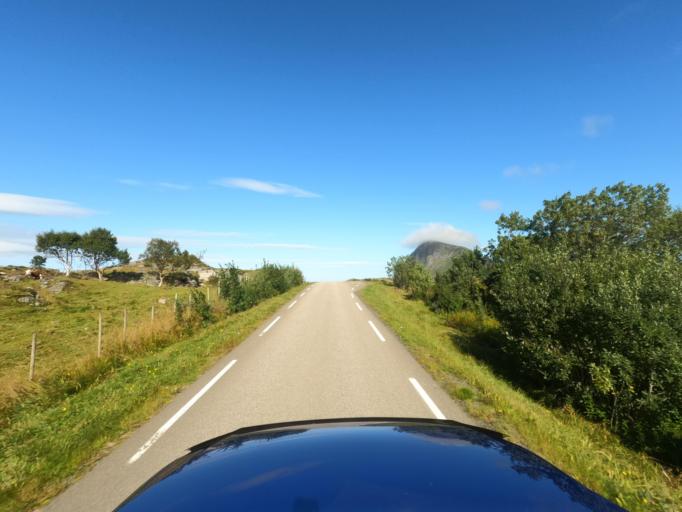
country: NO
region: Nordland
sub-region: Vestvagoy
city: Evjen
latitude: 68.3073
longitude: 14.0979
